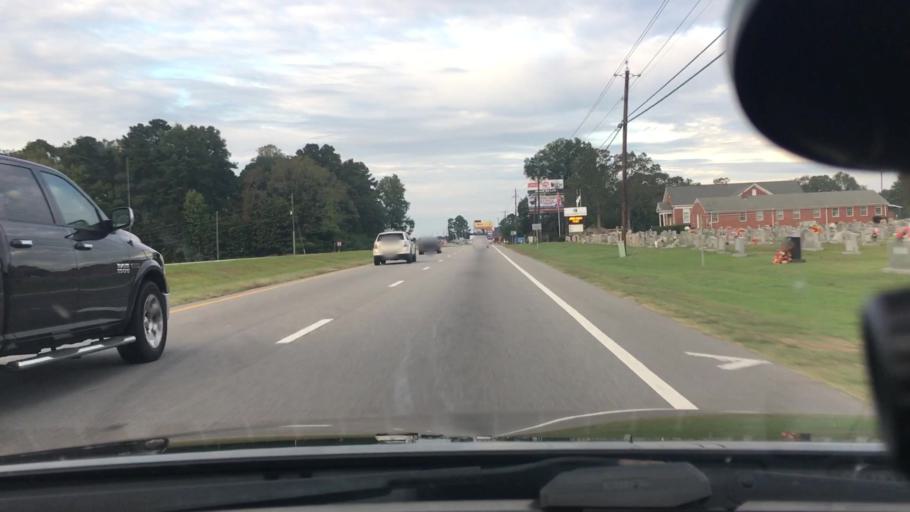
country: US
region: North Carolina
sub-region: Lee County
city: Sanford
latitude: 35.4270
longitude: -79.2233
